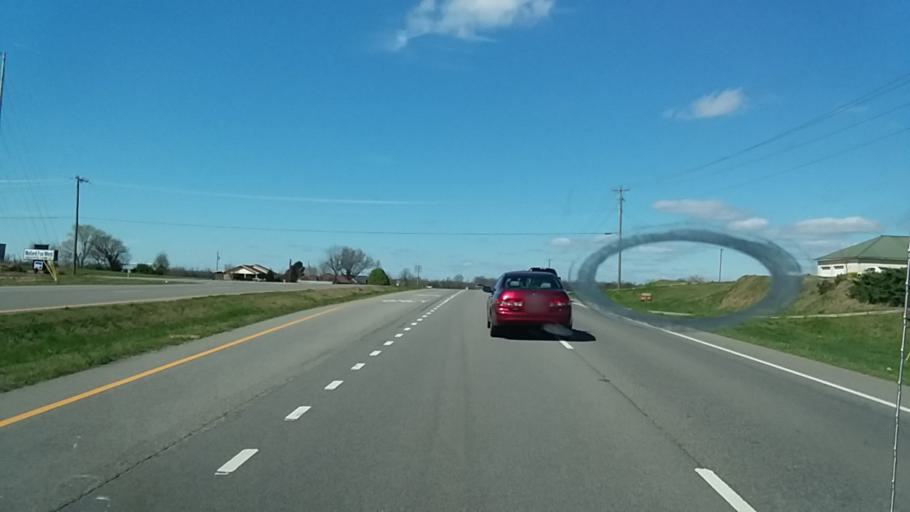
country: US
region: Alabama
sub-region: Morgan County
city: Trinity
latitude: 34.6348
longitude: -87.1124
